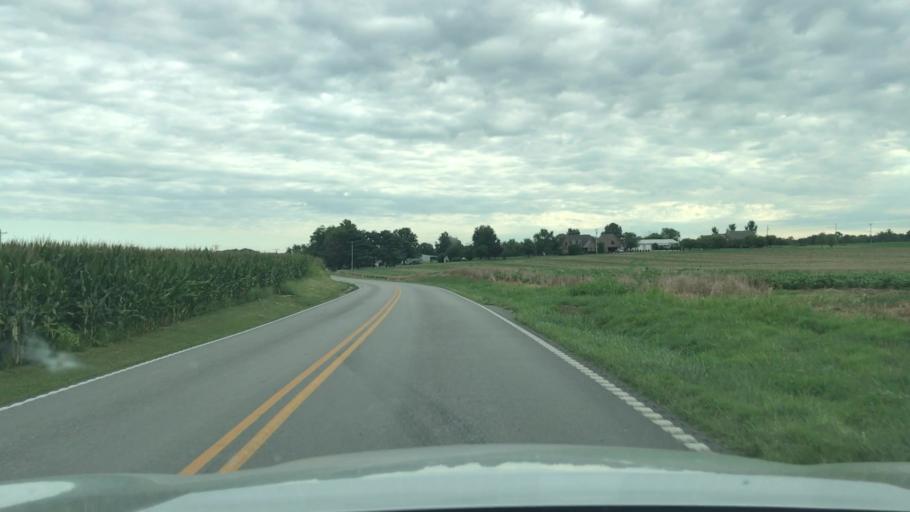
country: US
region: Kentucky
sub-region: Todd County
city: Guthrie
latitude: 36.7063
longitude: -87.1952
